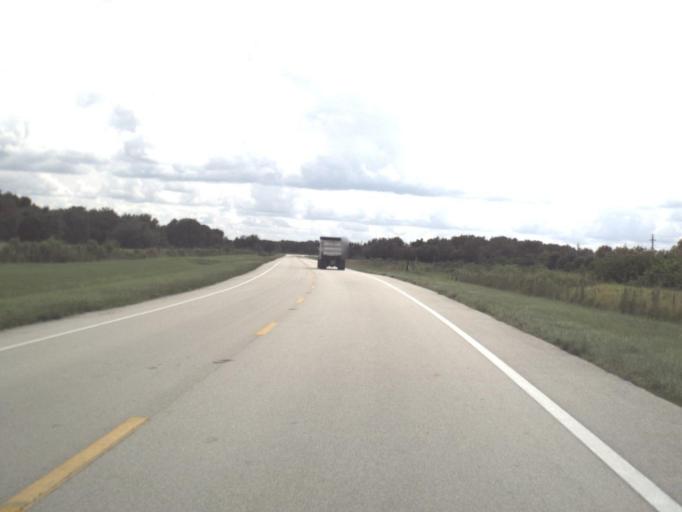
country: US
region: Florida
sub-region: DeSoto County
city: Southeast Arcadia
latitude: 27.1255
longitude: -81.7962
